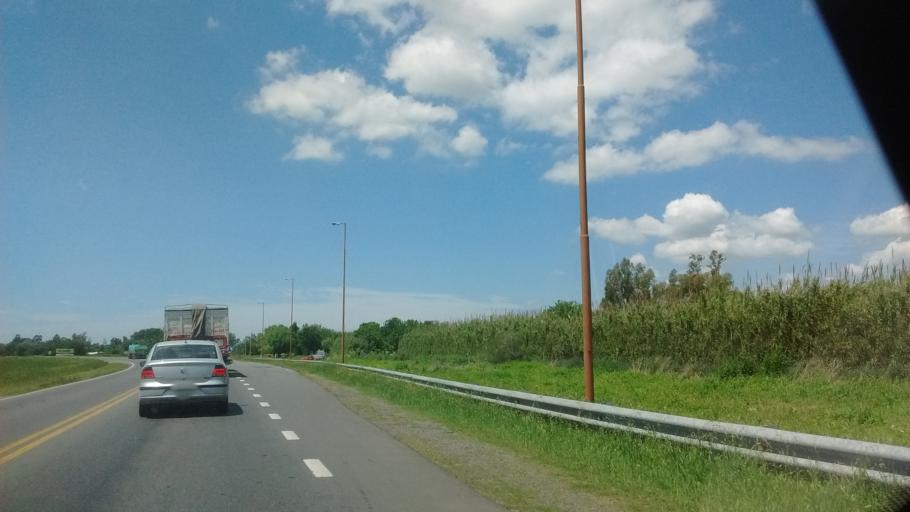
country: AR
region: Santa Fe
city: Funes
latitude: -32.8457
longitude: -60.7997
